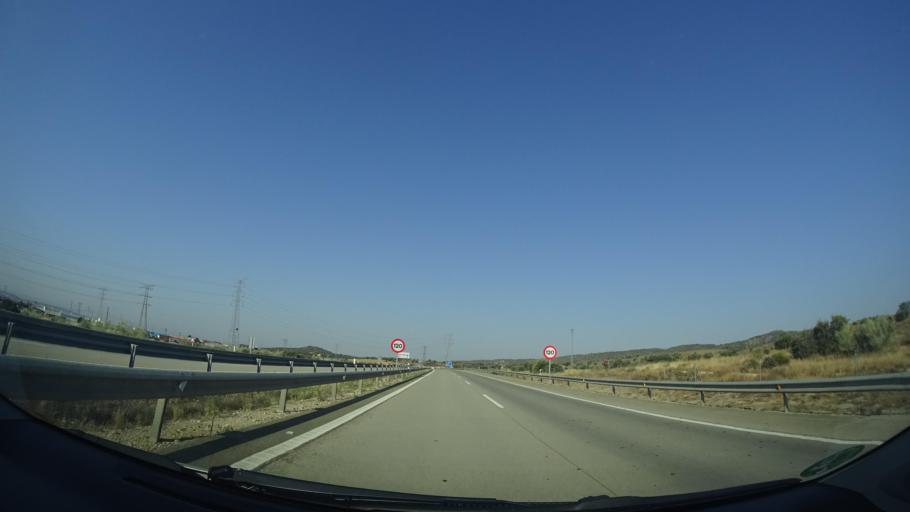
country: ES
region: Castille-La Mancha
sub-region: Province of Toledo
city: Talavera de la Reina
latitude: 40.0060
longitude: -4.8245
